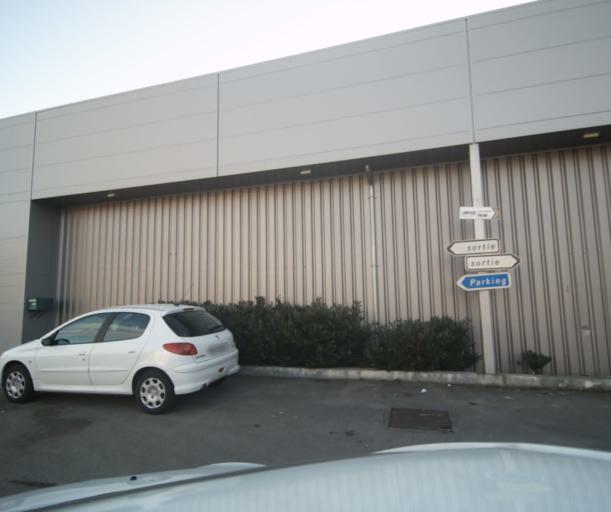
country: FR
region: Franche-Comte
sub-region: Departement du Doubs
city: Besancon
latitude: 47.2562
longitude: 6.0120
